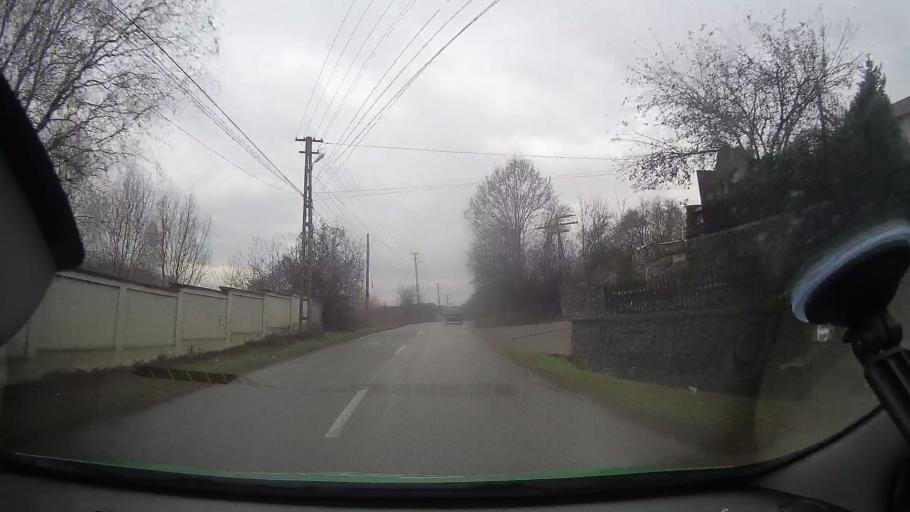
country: RO
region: Arad
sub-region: Comuna Gurahont
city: Gurahont
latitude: 46.2651
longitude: 22.3422
